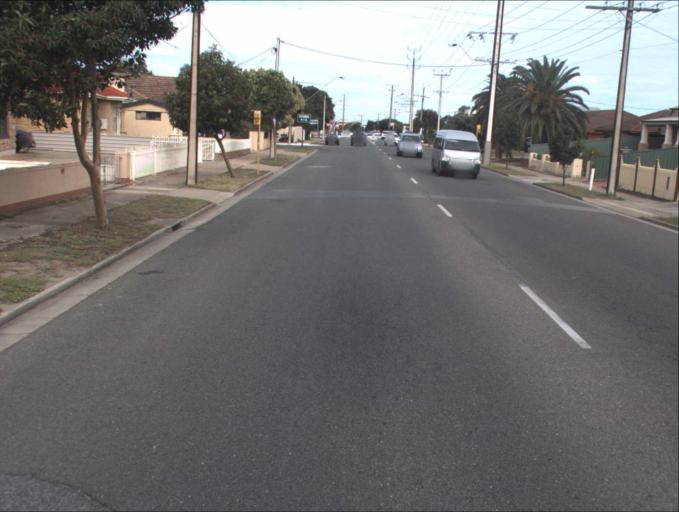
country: AU
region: South Australia
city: Port Adelaide
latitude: -34.8486
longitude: 138.4802
